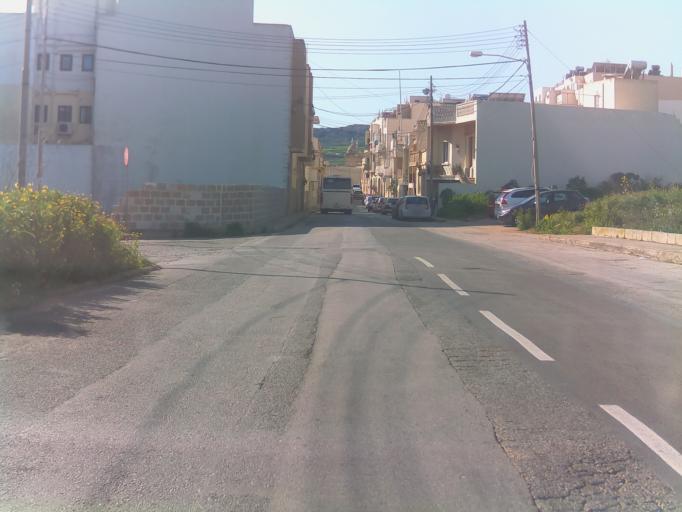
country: MT
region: L-Imgarr
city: Imgarr
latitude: 35.9238
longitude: 14.3672
